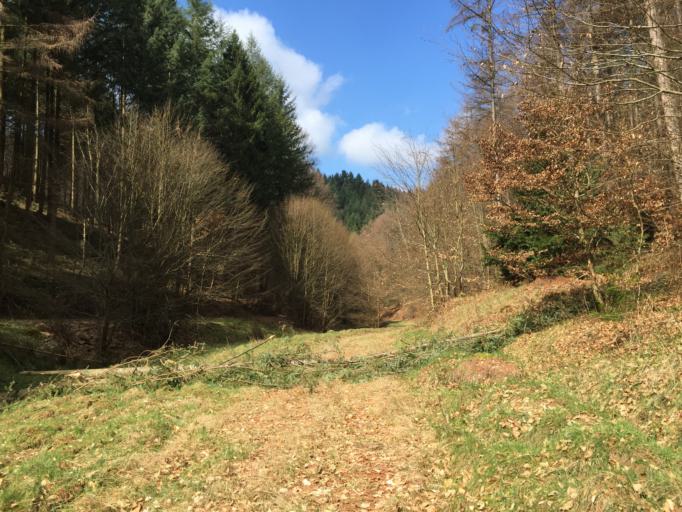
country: DE
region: Rheinland-Pfalz
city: Elmstein
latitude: 49.3982
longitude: 7.9269
